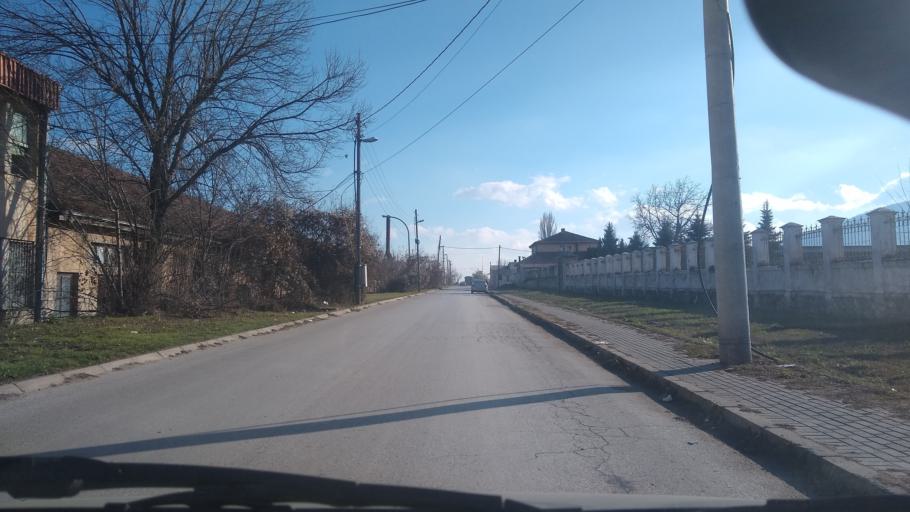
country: MK
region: Bitola
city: Bitola
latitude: 41.0146
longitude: 21.3450
